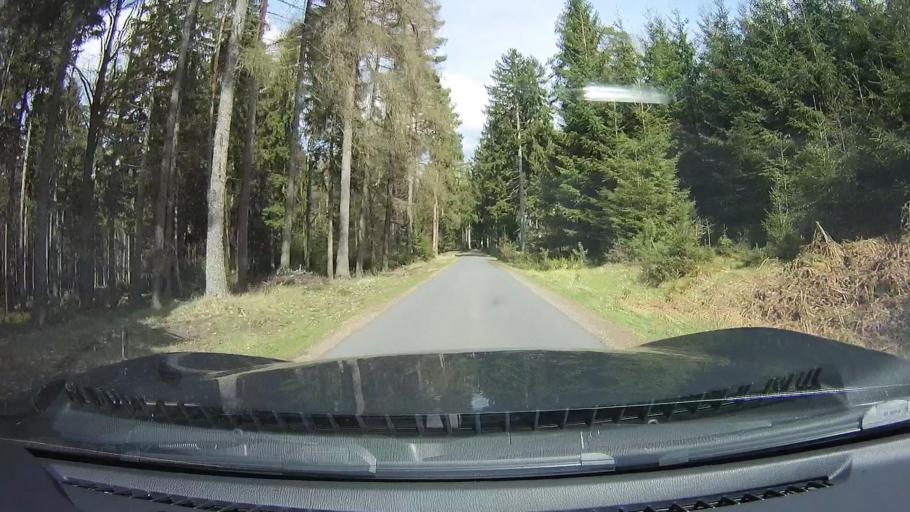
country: DE
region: Hesse
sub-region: Regierungsbezirk Darmstadt
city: Hesseneck
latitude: 49.6223
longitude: 9.0778
